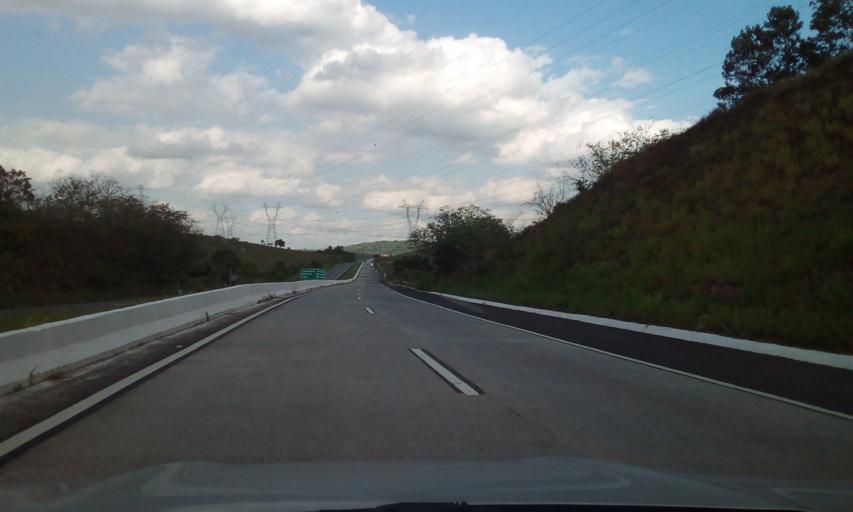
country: BR
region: Pernambuco
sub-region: Joaquim Nabuco
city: Joaquim Nabuco
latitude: -8.5934
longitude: -35.5226
